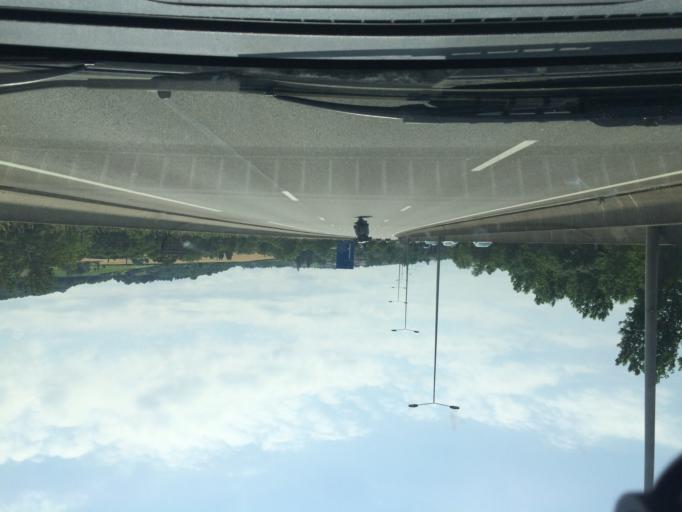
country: FR
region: Rhone-Alpes
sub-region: Departement du Rhone
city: Villefranche-sur-Saone
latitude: 45.9582
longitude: 4.7188
